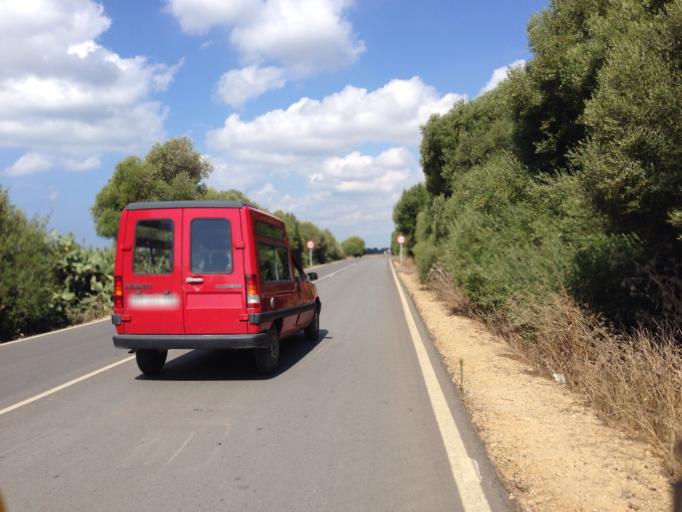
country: ES
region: Andalusia
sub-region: Provincia de Cadiz
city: Vejer de la Frontera
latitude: 36.2174
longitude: -6.0380
